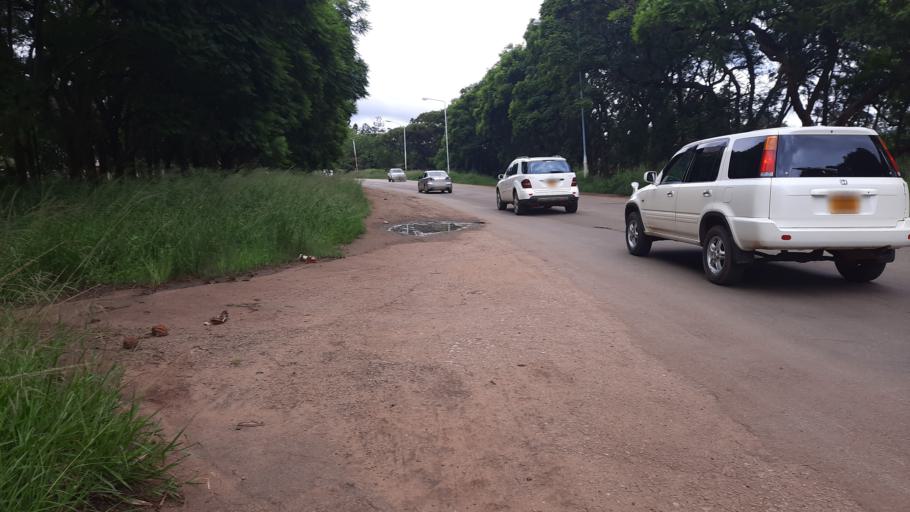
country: ZW
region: Harare
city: Harare
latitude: -17.8204
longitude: 31.0279
